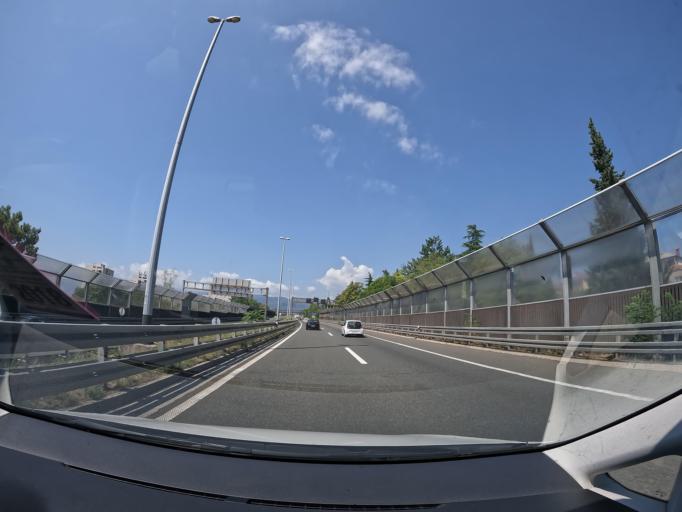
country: HR
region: Primorsko-Goranska
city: Klana
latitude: 45.5355
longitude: 14.3867
